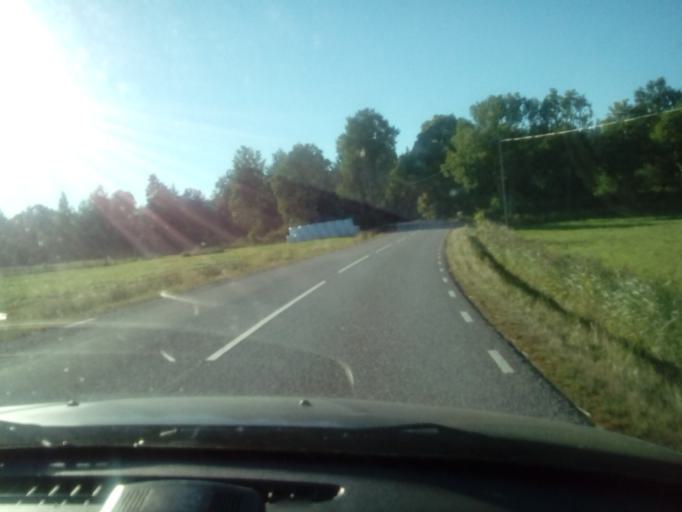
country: SE
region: Kalmar
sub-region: Vasterviks Kommun
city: Gamleby
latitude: 57.7879
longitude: 16.3902
